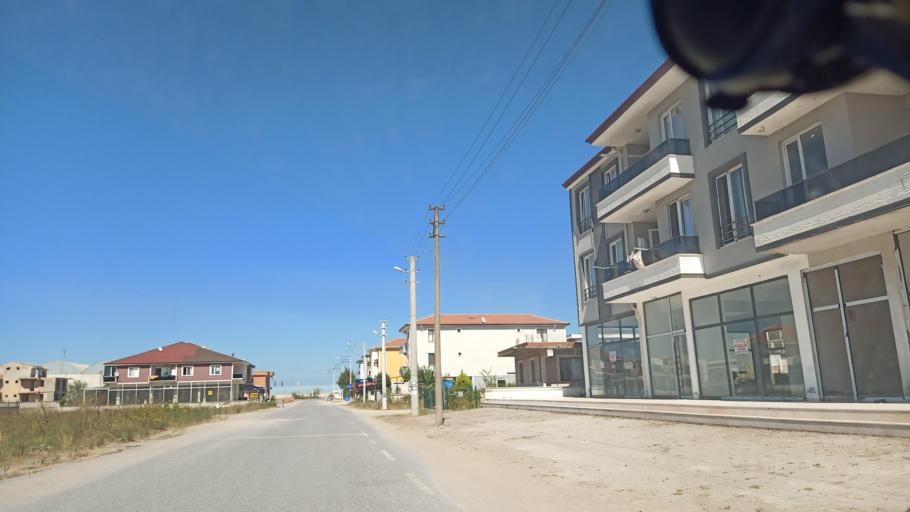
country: TR
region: Sakarya
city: Karasu
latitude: 41.1150
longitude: 30.6730
